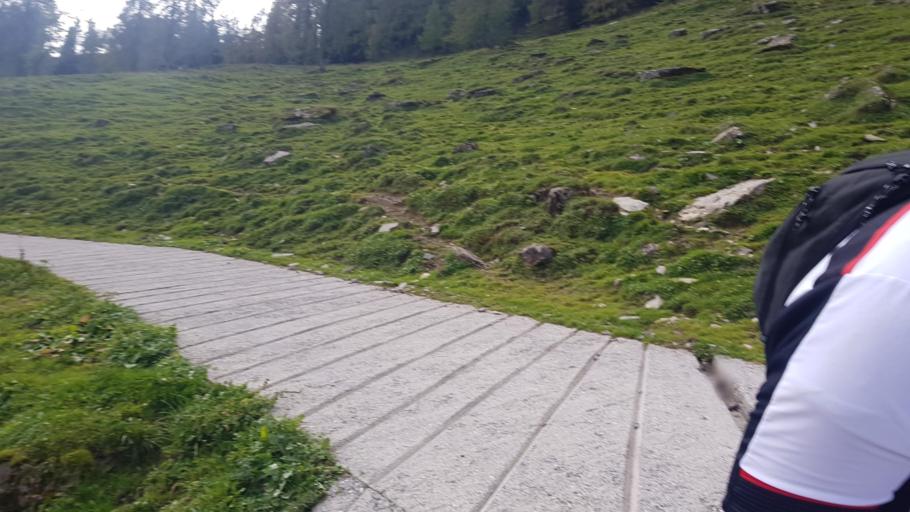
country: IT
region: Friuli Venezia Giulia
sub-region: Provincia di Udine
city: Sauris di Sotto
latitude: 46.5030
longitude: 12.7376
